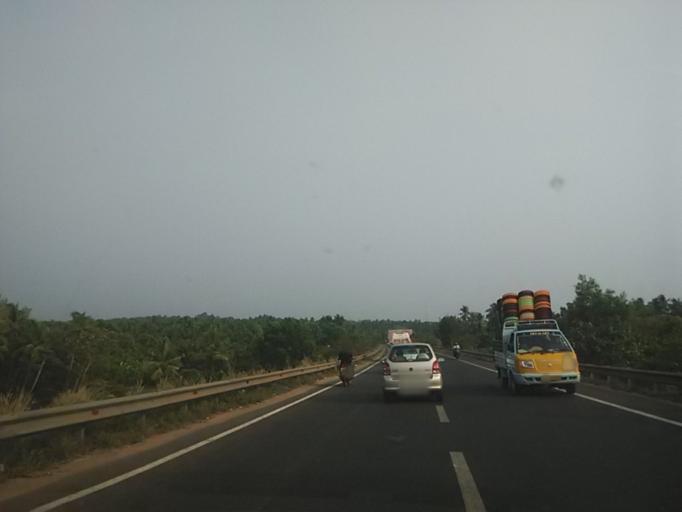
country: IN
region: Kerala
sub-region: Kozhikode
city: Kozhikode
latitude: 11.2995
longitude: 75.7939
